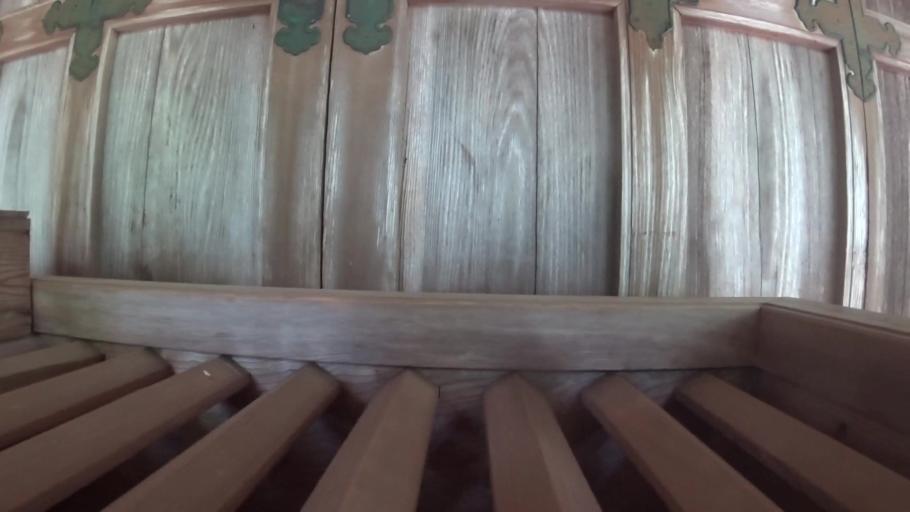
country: JP
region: Kyoto
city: Maizuru
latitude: 35.3898
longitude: 135.4422
